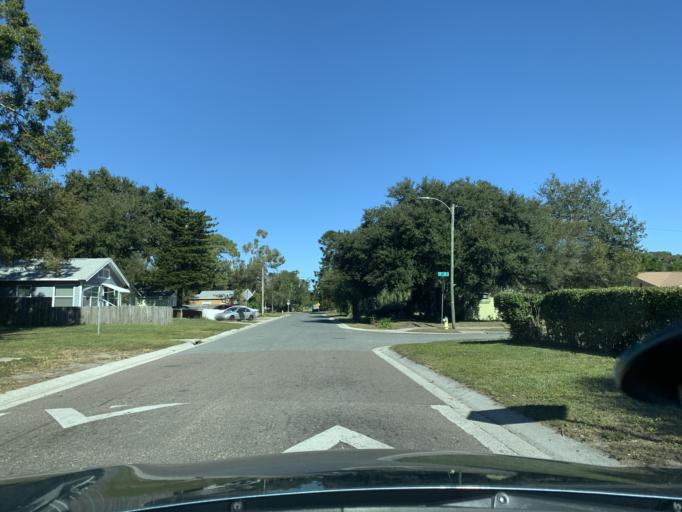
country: US
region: Florida
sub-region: Pinellas County
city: Gulfport
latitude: 27.7508
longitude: -82.6976
